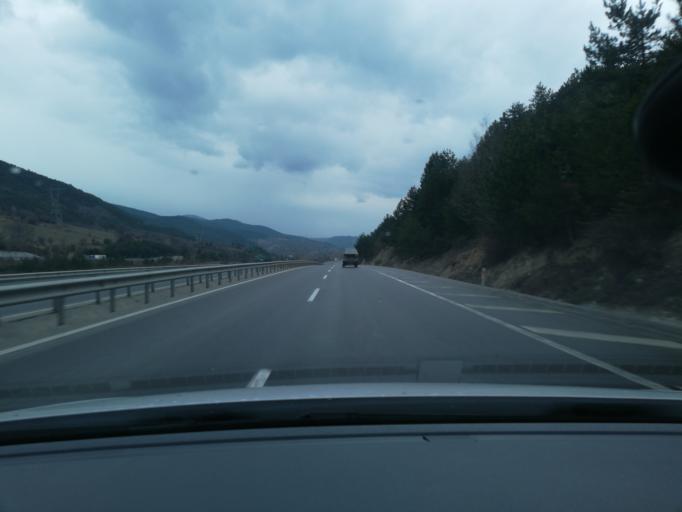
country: TR
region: Bolu
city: Yenicaga
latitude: 40.7483
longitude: 31.8830
